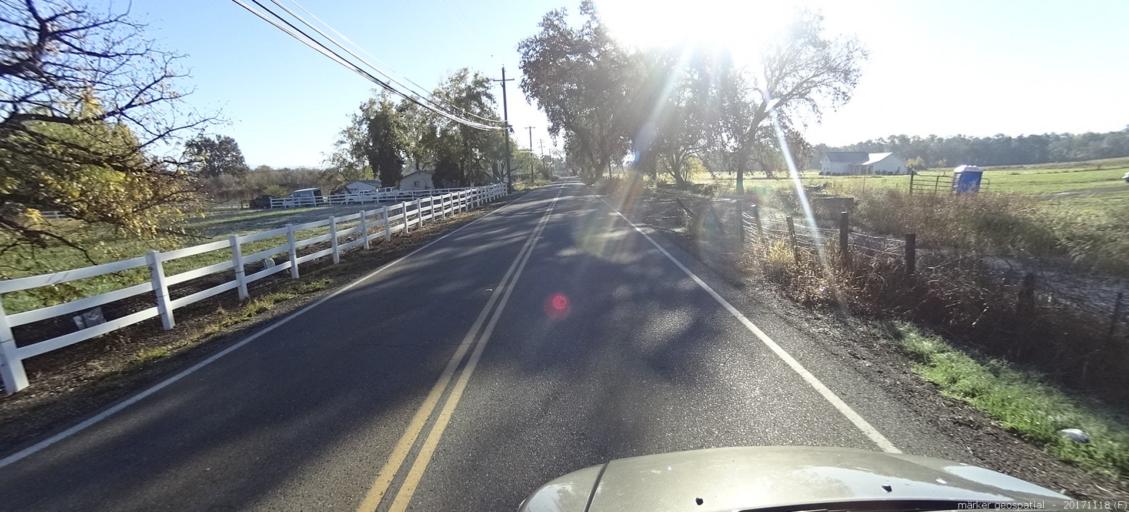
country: US
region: California
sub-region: Shasta County
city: Anderson
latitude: 40.4493
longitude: -122.2641
